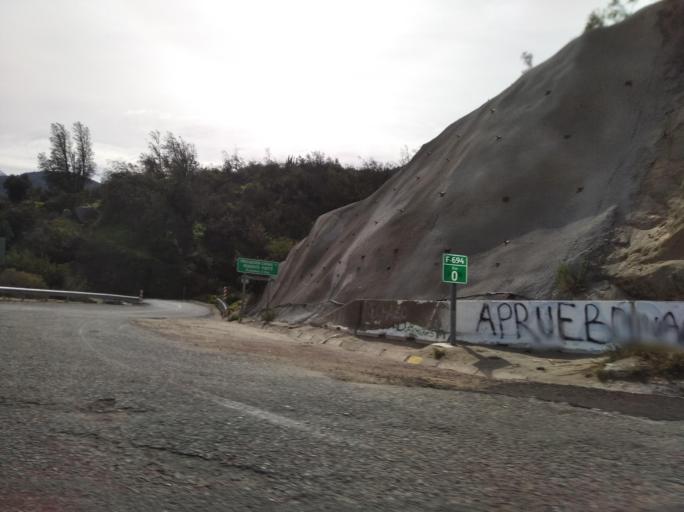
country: CL
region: Valparaiso
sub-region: Provincia de San Felipe
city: Llaillay
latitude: -33.0583
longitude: -71.0182
